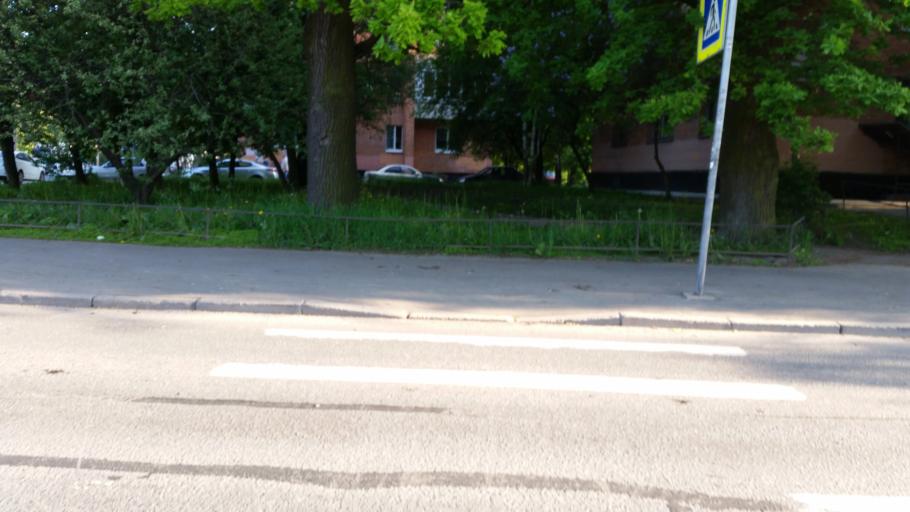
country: RU
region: St.-Petersburg
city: Sosnovaya Polyana
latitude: 59.8449
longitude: 30.1465
